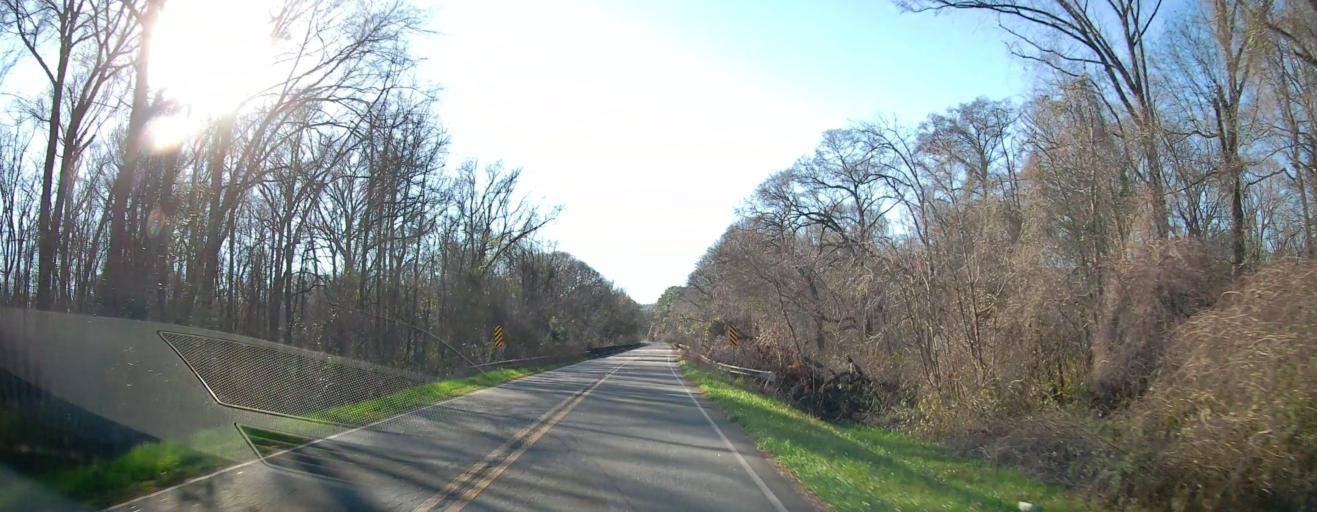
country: US
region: Georgia
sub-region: Sumter County
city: Americus
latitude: 32.0066
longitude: -84.2252
